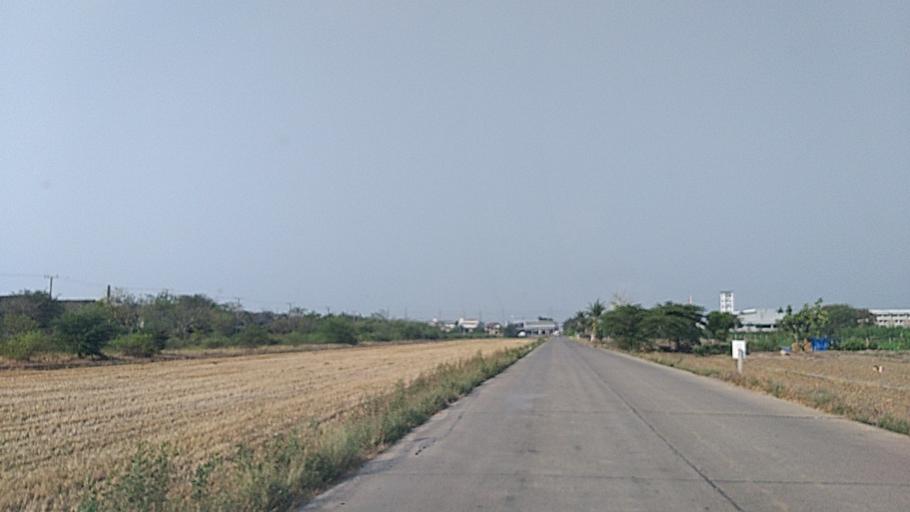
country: TH
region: Nonthaburi
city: Sai Noi
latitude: 13.9780
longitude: 100.3213
